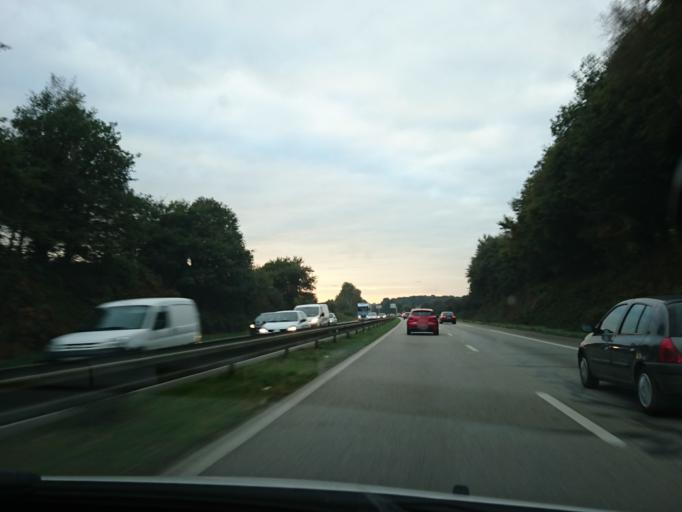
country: FR
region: Brittany
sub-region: Departement du Morbihan
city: Hennebont
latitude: 47.7896
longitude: -3.2664
